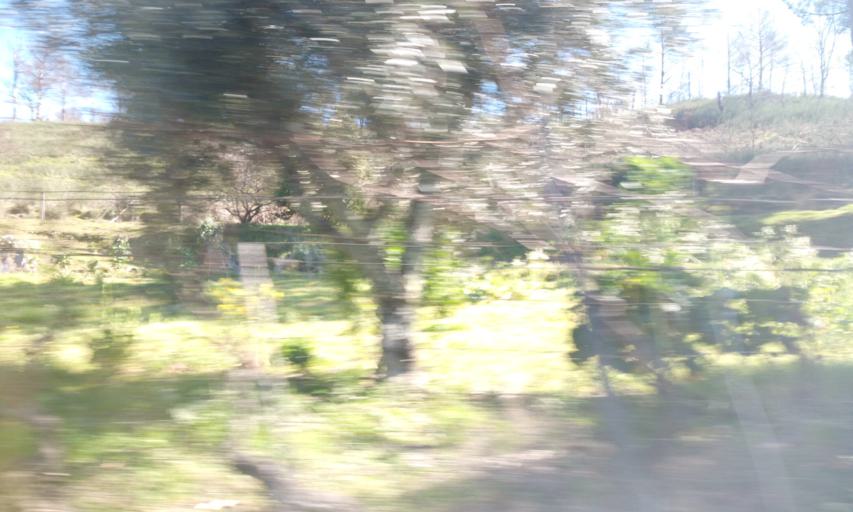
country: PT
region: Guarda
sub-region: Manteigas
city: Manteigas
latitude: 40.4786
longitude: -7.6170
